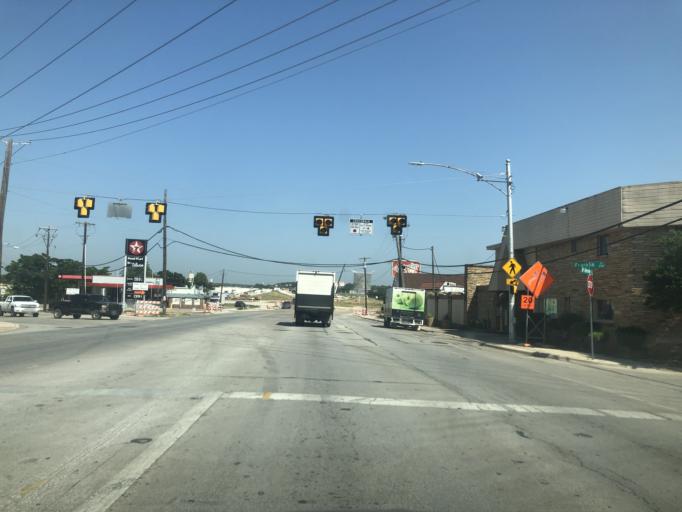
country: US
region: Texas
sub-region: Tarrant County
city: Fort Worth
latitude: 32.7587
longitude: -97.3431
